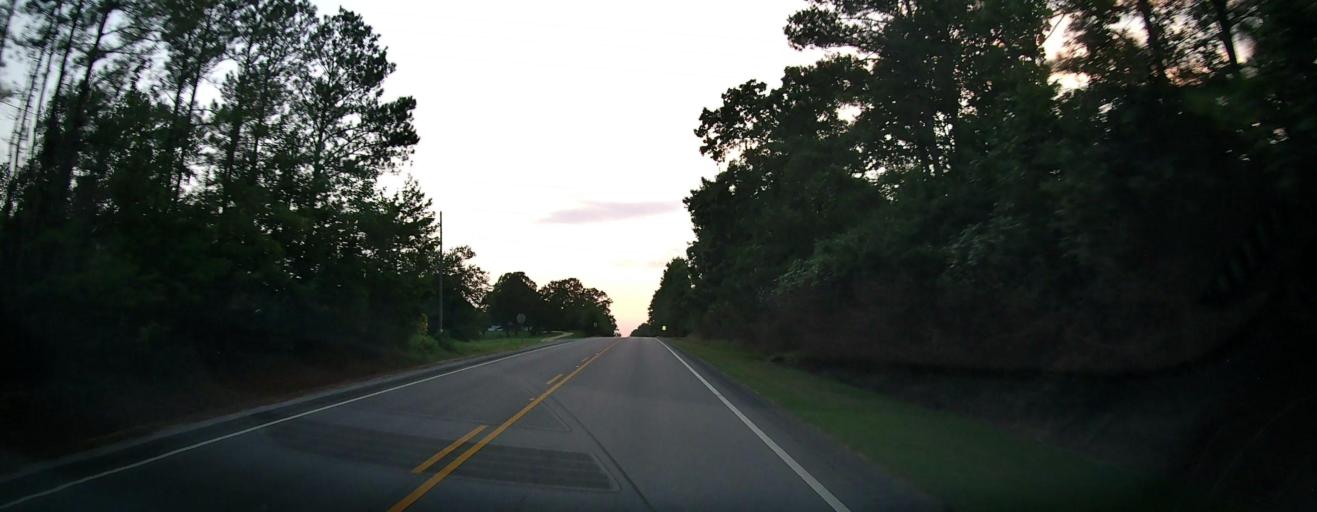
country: US
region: Alabama
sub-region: Marion County
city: Hamilton
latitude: 34.1375
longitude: -88.0079
